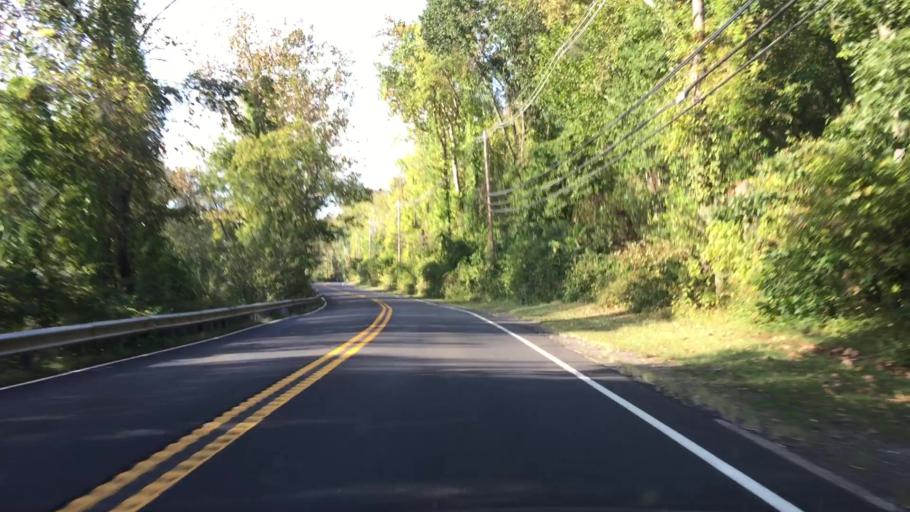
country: US
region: Pennsylvania
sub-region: Bucks County
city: New Hope
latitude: 40.3939
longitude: -74.9614
